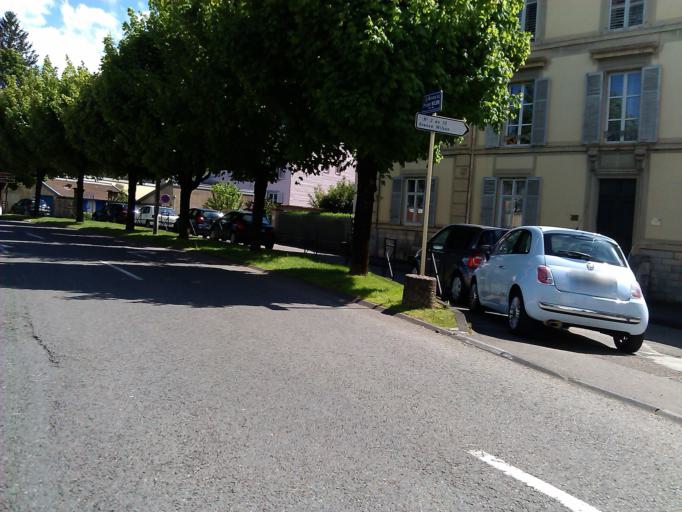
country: FR
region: Franche-Comte
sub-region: Departement du Doubs
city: Arbouans
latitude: 47.5076
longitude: 6.7960
